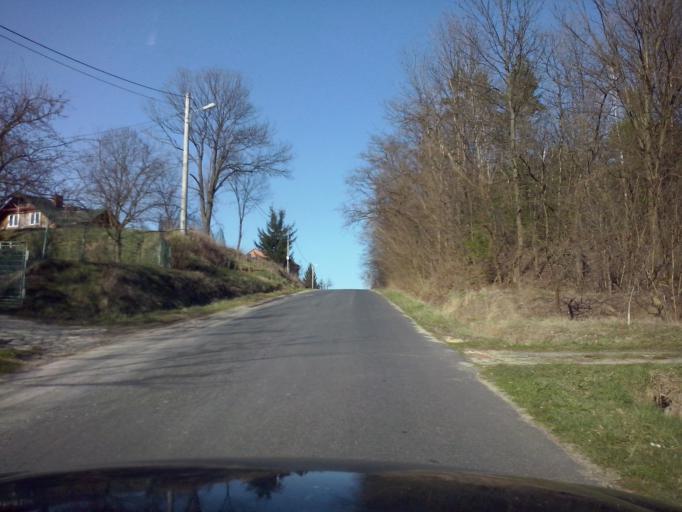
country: PL
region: Subcarpathian Voivodeship
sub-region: Powiat nizanski
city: Krzeszow
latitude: 50.3898
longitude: 22.3795
